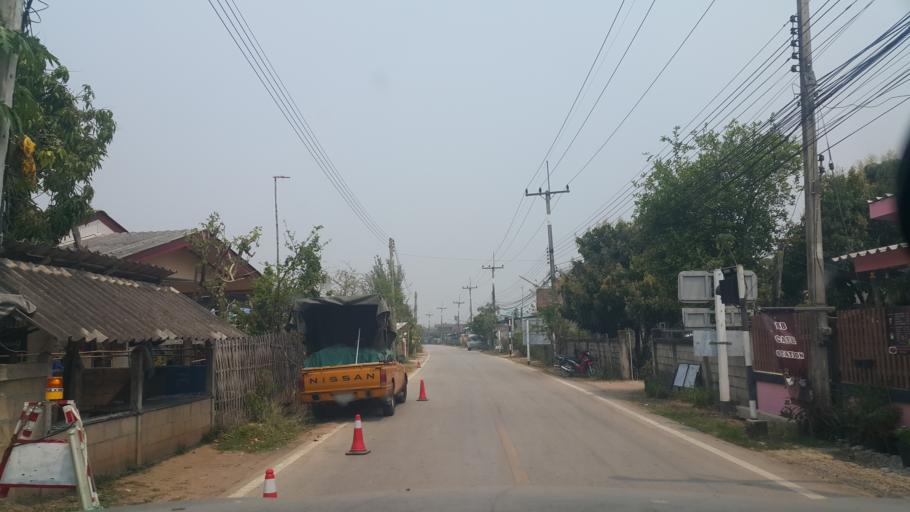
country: TH
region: Lampang
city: Hang Chat
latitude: 18.2490
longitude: 99.2346
